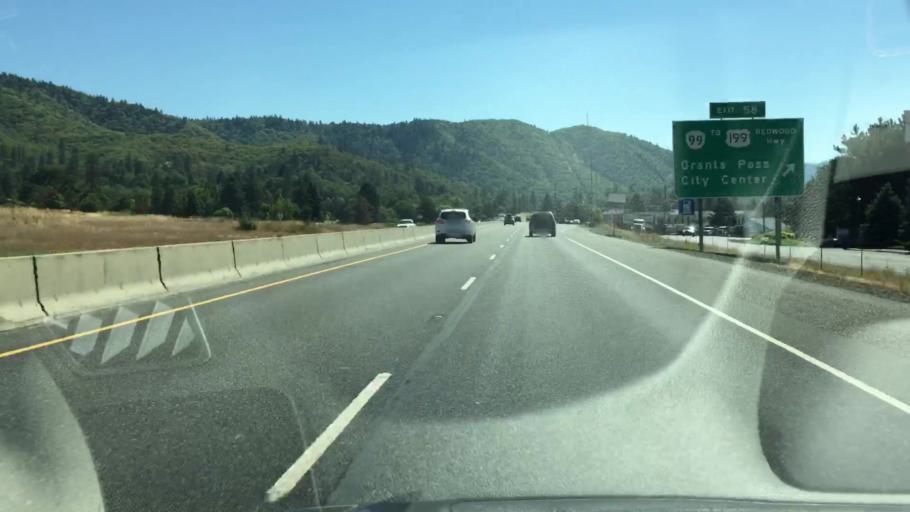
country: US
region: Oregon
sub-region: Josephine County
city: Grants Pass
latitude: 42.4664
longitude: -123.3274
